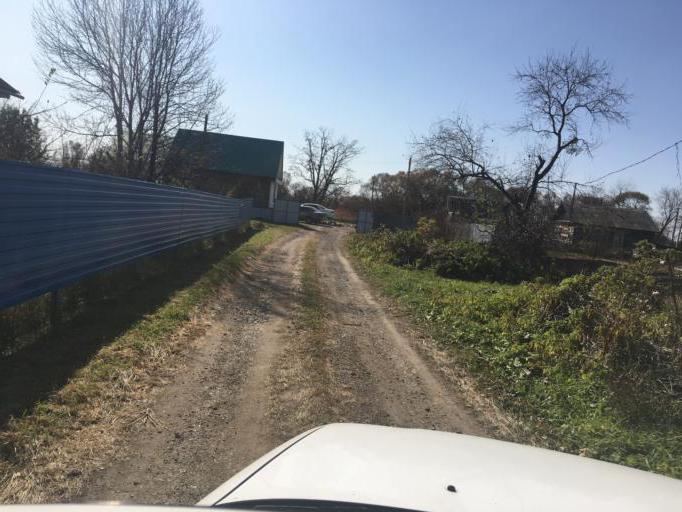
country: RU
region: Primorskiy
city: Dal'nerechensk
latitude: 45.9083
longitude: 133.7953
